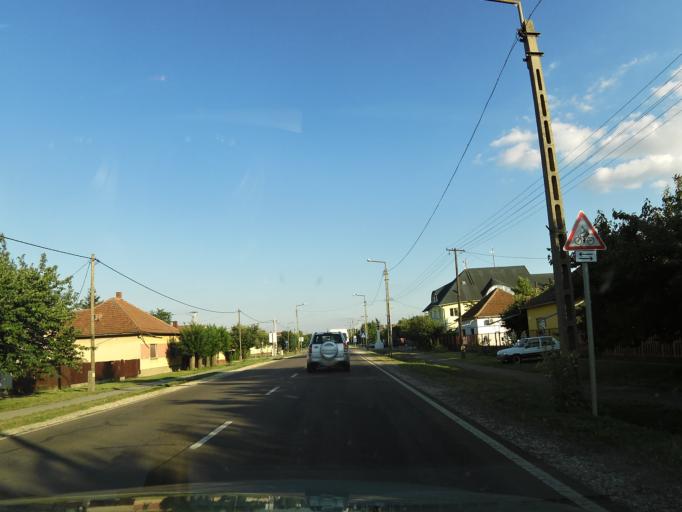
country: HU
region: Jasz-Nagykun-Szolnok
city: Rakocziujfalu
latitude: 47.0615
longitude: 20.2602
